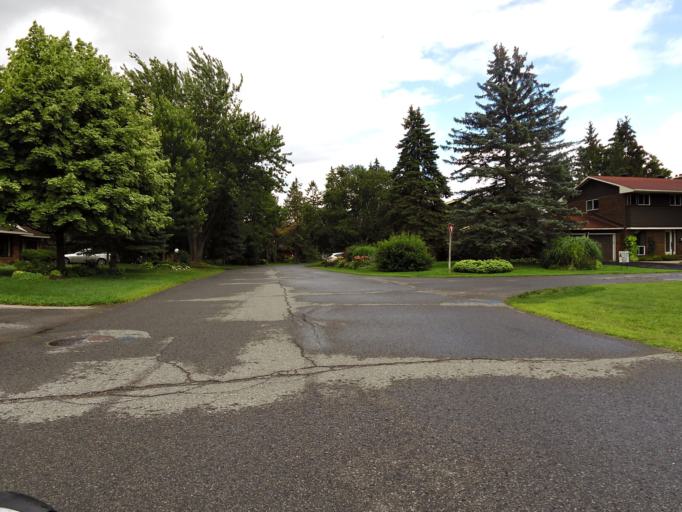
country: CA
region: Ontario
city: Bells Corners
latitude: 45.3342
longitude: -75.9108
